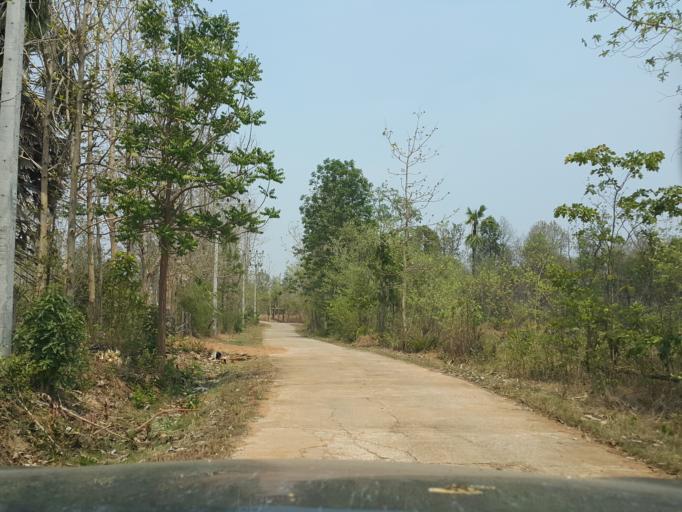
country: TH
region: Lampang
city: Mae Phrik
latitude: 17.5656
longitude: 99.0903
